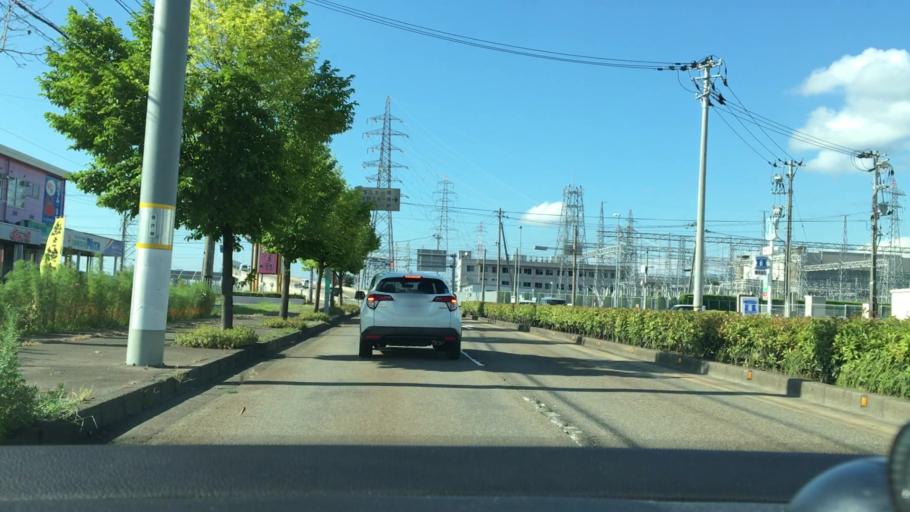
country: JP
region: Fukui
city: Fukui-shi
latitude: 36.0889
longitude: 136.2825
